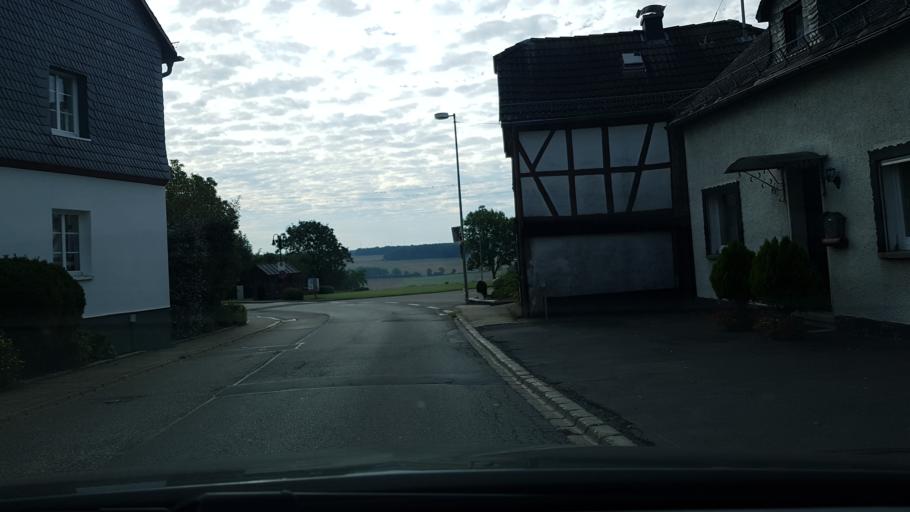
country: DE
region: Rheinland-Pfalz
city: Mermuth
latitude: 50.1588
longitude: 7.4852
